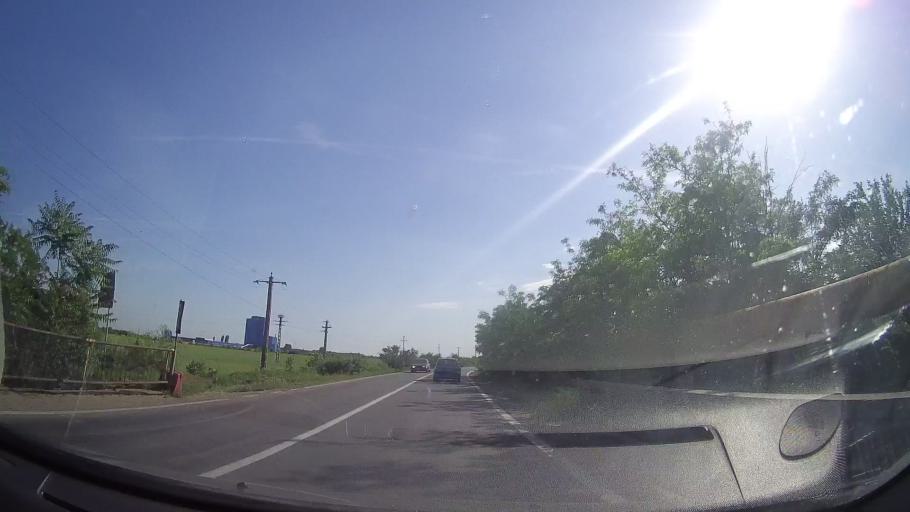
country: RO
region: Prahova
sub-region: Comuna Berceni
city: Corlatesti
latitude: 44.9122
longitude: 26.0847
